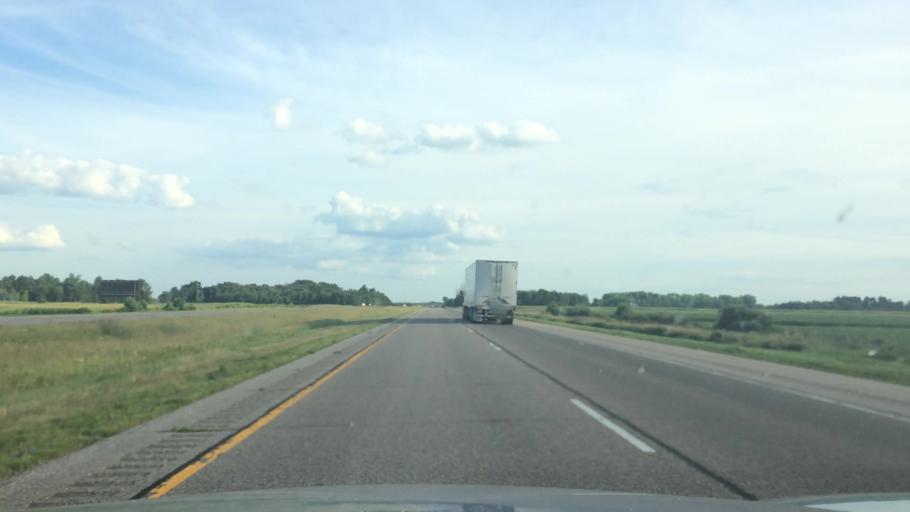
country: US
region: Wisconsin
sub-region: Portage County
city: Plover
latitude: 44.3834
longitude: -89.5199
